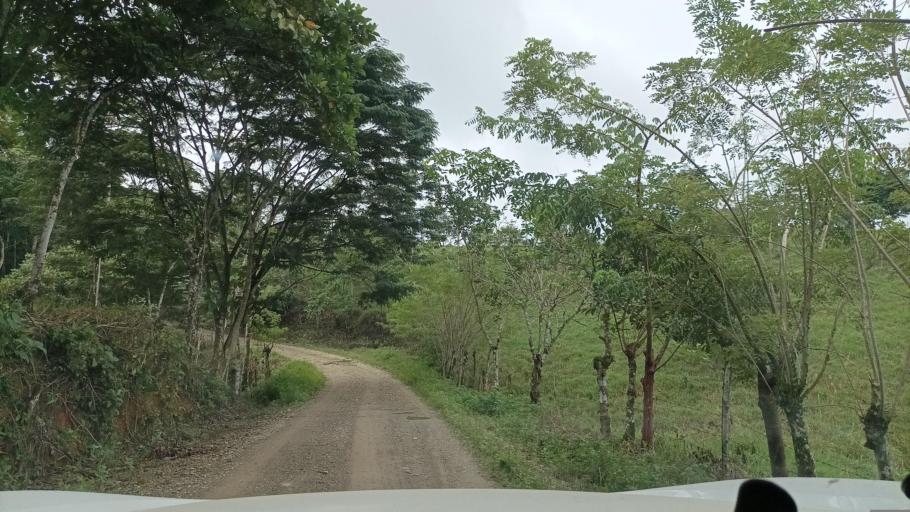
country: MX
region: Veracruz
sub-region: Uxpanapa
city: Poblado 10
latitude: 17.4321
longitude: -94.4176
